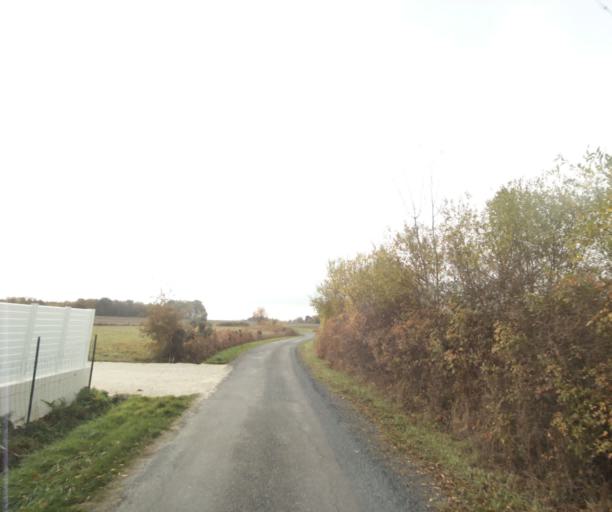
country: FR
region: Poitou-Charentes
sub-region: Departement de la Charente-Maritime
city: Saint-Georges-des-Coteaux
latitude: 45.7866
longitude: -0.7229
